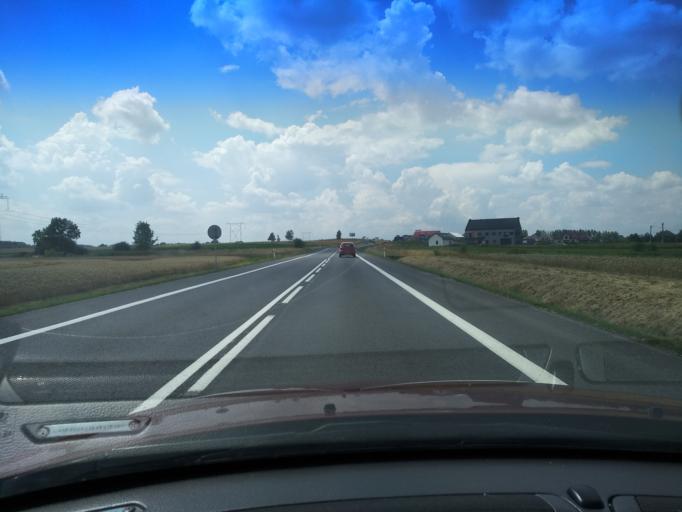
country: PL
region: Lower Silesian Voivodeship
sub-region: Powiat lubanski
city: Luban
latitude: 51.1336
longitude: 15.2650
